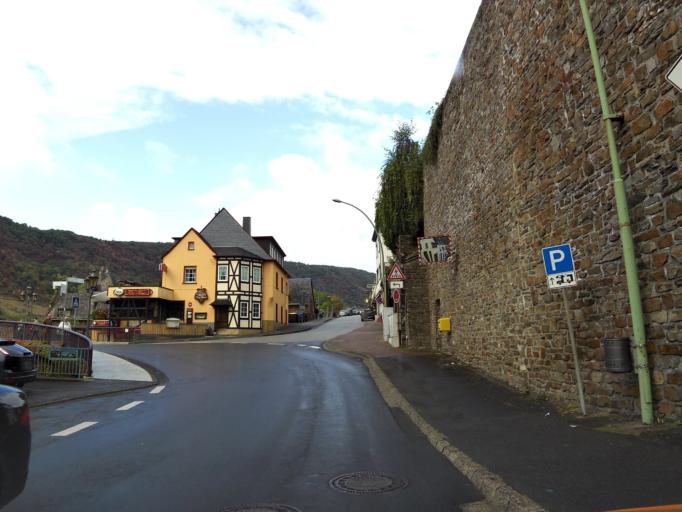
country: DE
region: Rheinland-Pfalz
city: Cochem
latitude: 50.1471
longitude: 7.1702
